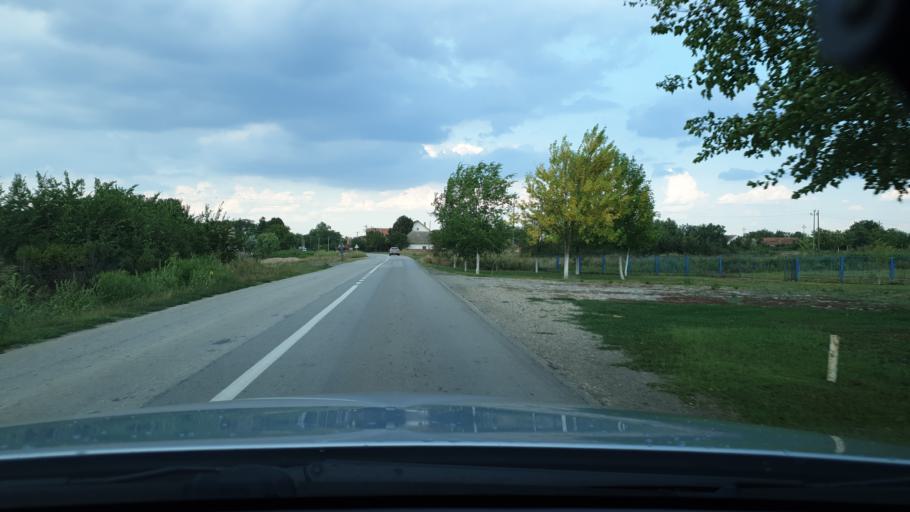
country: RS
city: Boka
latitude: 45.3474
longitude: 20.8255
